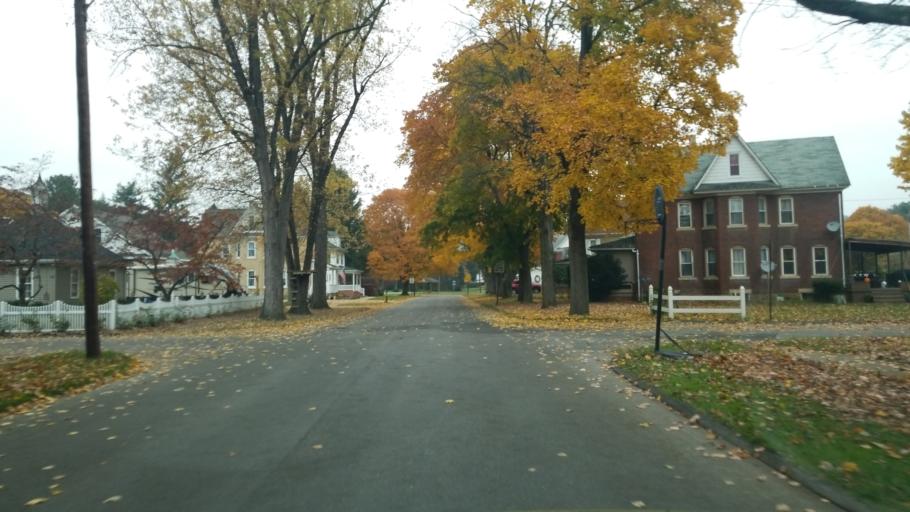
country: US
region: Pennsylvania
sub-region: Clearfield County
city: Clearfield
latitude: 41.0111
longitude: -78.4468
